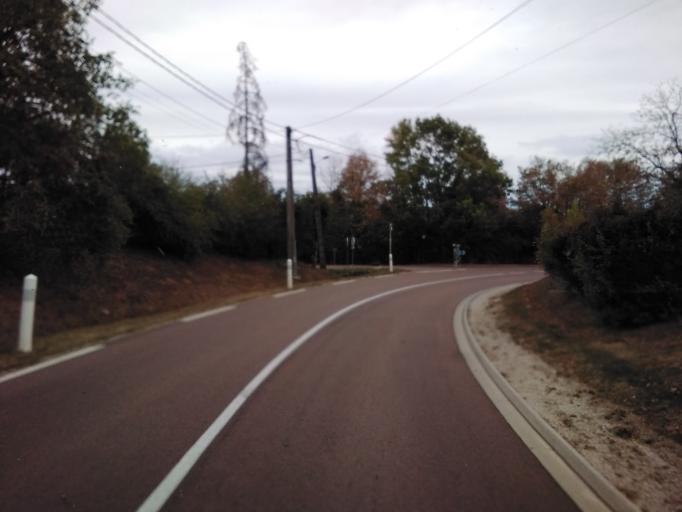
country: FR
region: Champagne-Ardenne
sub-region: Departement de l'Aube
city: Vendeuvre-sur-Barse
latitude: 48.1973
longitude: 4.4395
